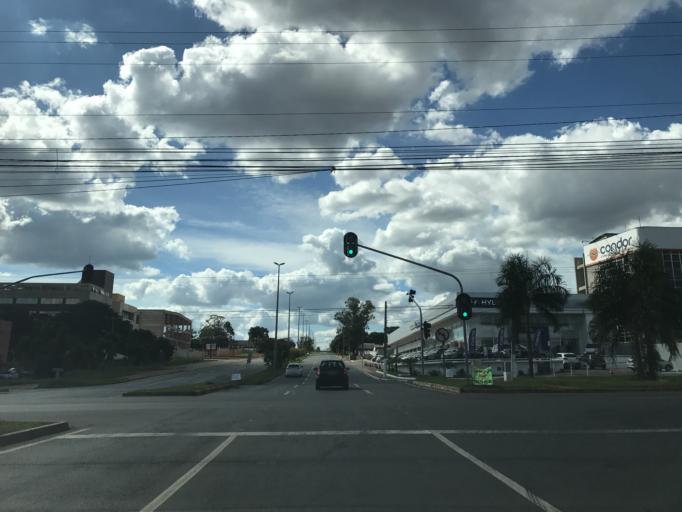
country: BR
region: Federal District
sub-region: Brasilia
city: Brasilia
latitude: -15.8051
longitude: -47.9682
